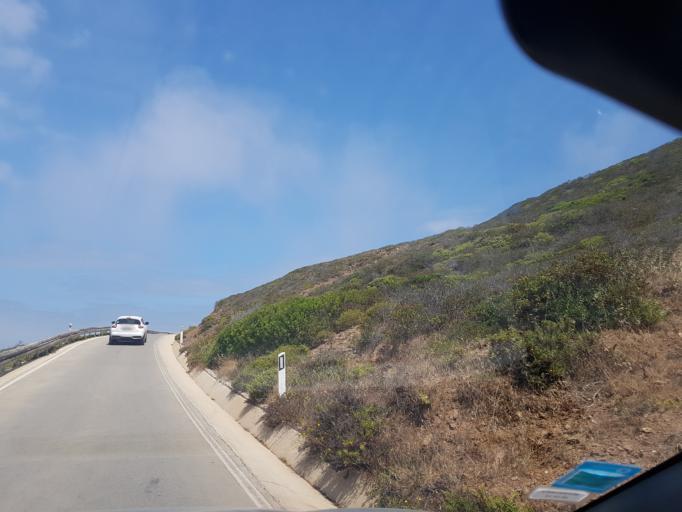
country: PT
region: Faro
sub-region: Vila do Bispo
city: Vila do Bispo
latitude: 37.1060
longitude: -8.9336
